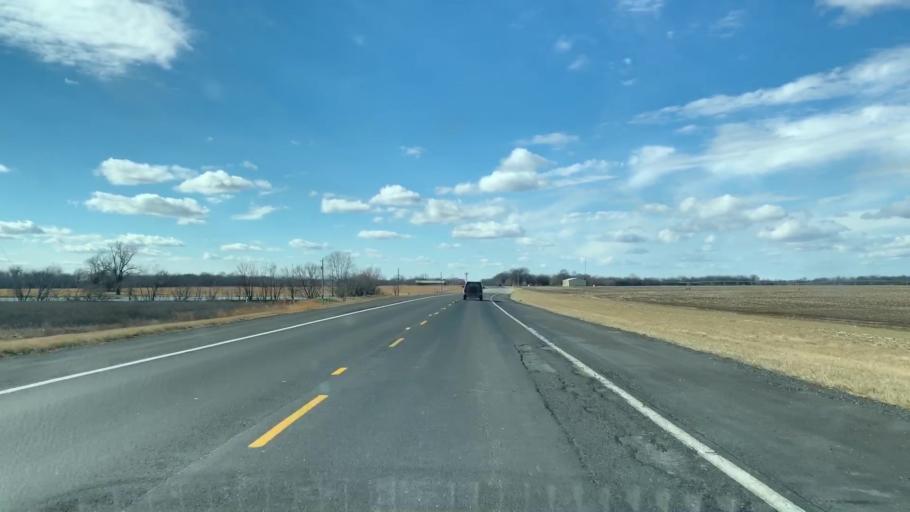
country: US
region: Kansas
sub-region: Labette County
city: Parsons
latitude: 37.3403
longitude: -95.1198
